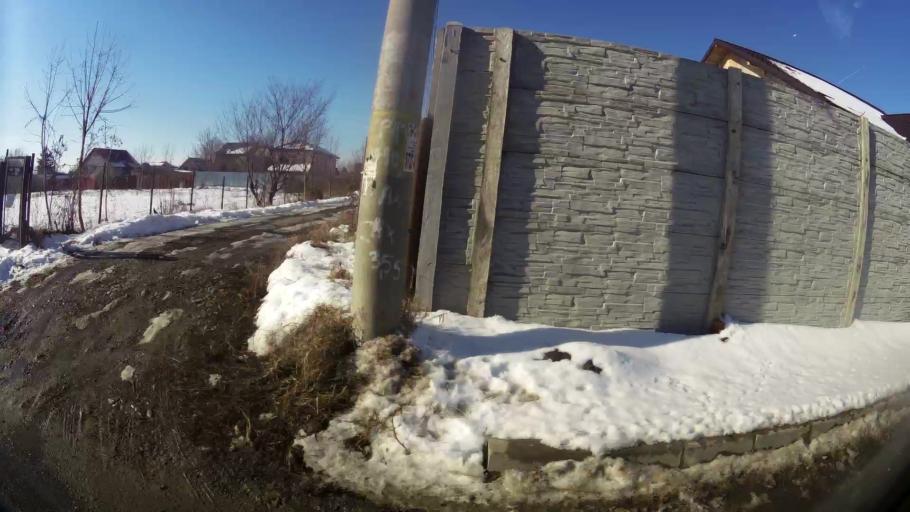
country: RO
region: Ilfov
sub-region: Comuna Magurele
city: Magurele
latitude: 44.3844
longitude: 26.0521
